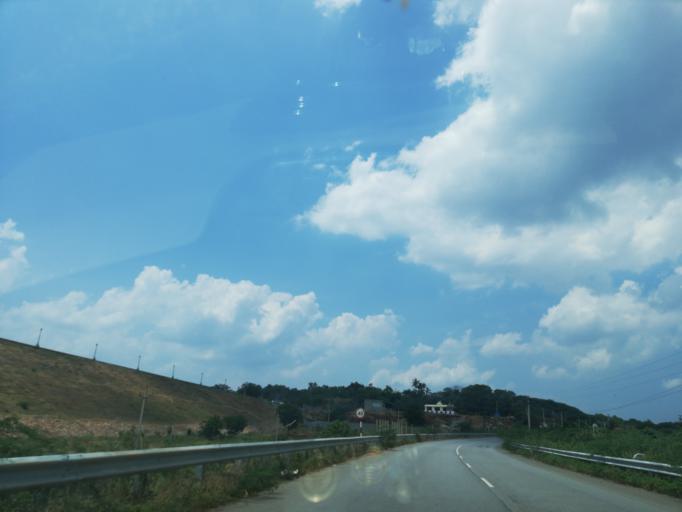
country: IN
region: Andhra Pradesh
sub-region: Guntur
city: Macherla
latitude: 16.5977
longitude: 79.3076
